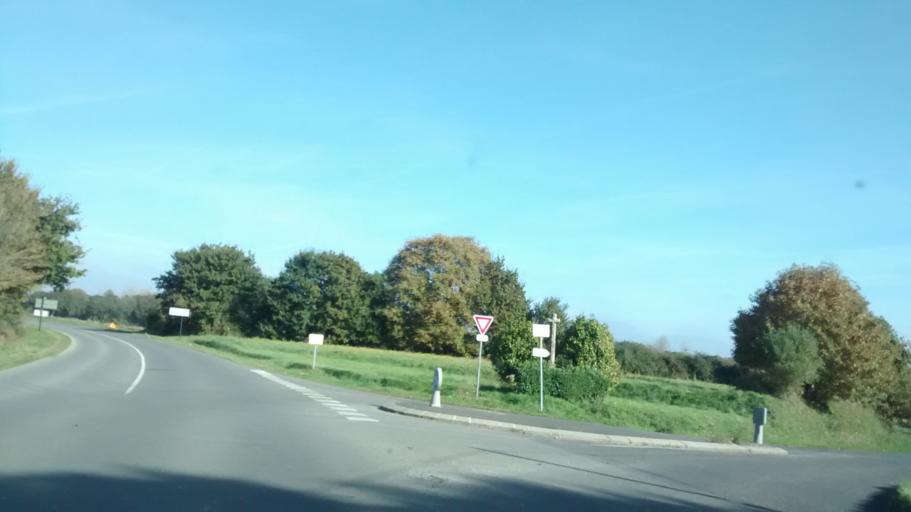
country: FR
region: Brittany
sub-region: Departement des Cotes-d'Armor
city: Saint-Quay-Perros
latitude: 48.7536
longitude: -3.4407
